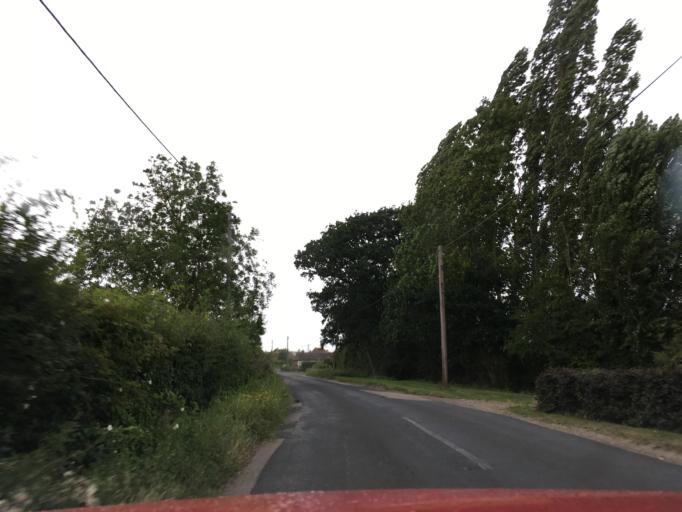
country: GB
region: England
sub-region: Kent
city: Marden
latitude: 51.1872
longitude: 0.4820
